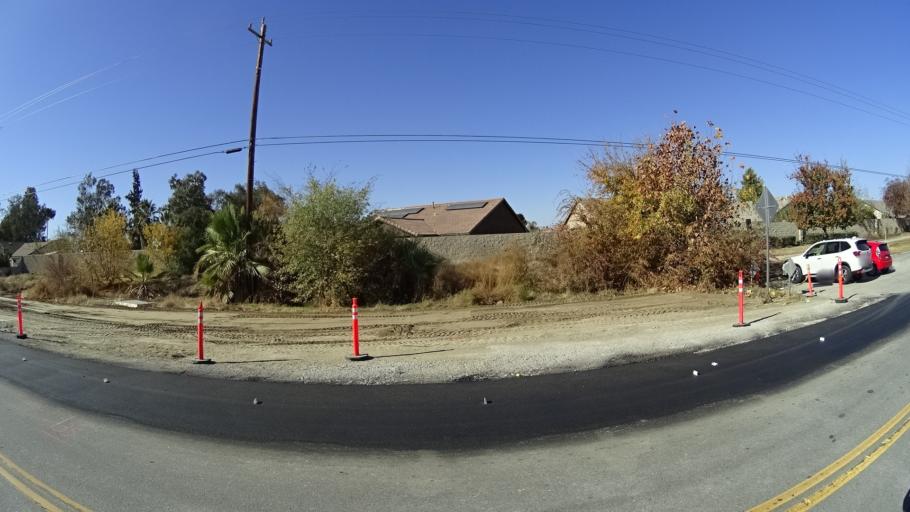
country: US
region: California
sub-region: Kern County
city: Greenfield
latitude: 35.2687
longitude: -119.0567
